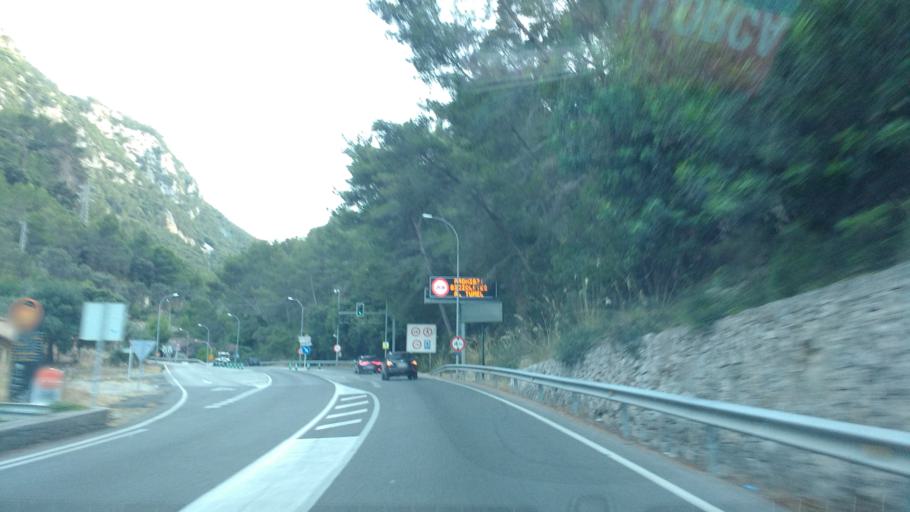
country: ES
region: Balearic Islands
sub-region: Illes Balears
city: Soller
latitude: 39.7468
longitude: 2.6981
